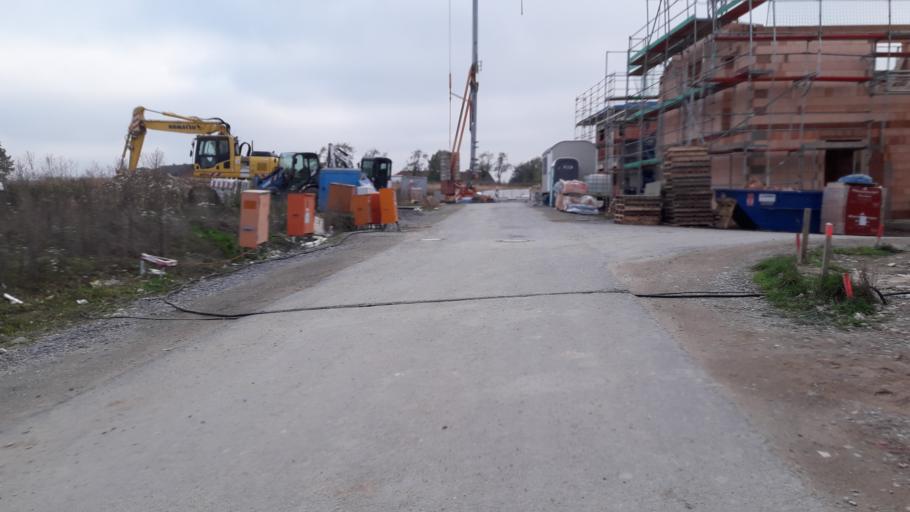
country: DE
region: North Rhine-Westphalia
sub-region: Regierungsbezirk Detmold
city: Paderborn
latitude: 51.6666
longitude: 8.7316
